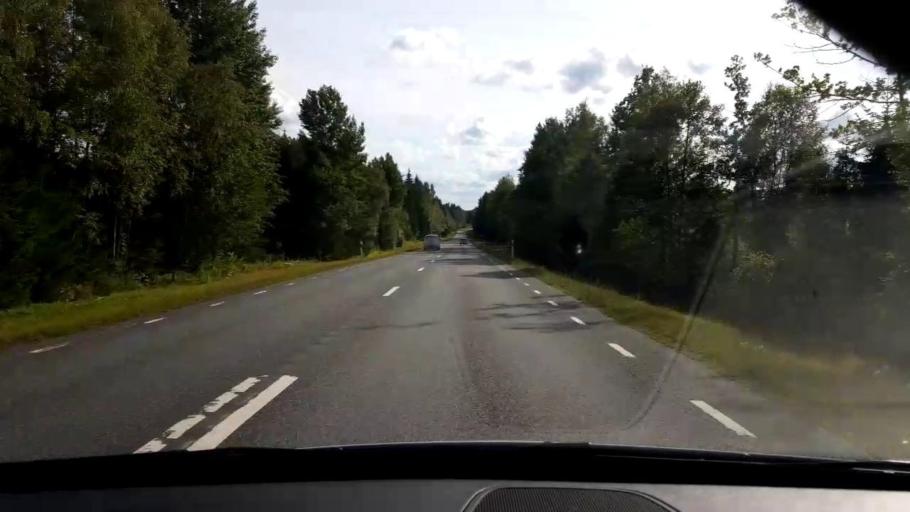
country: SE
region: Joenkoeping
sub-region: Savsjo Kommun
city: Vrigstad
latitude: 57.3365
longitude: 14.3561
